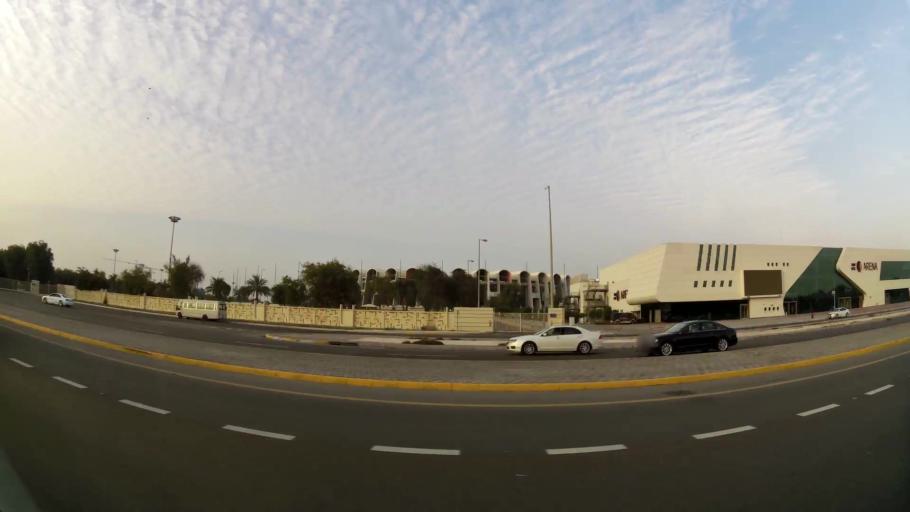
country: AE
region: Abu Dhabi
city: Abu Dhabi
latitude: 24.4128
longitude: 54.4525
